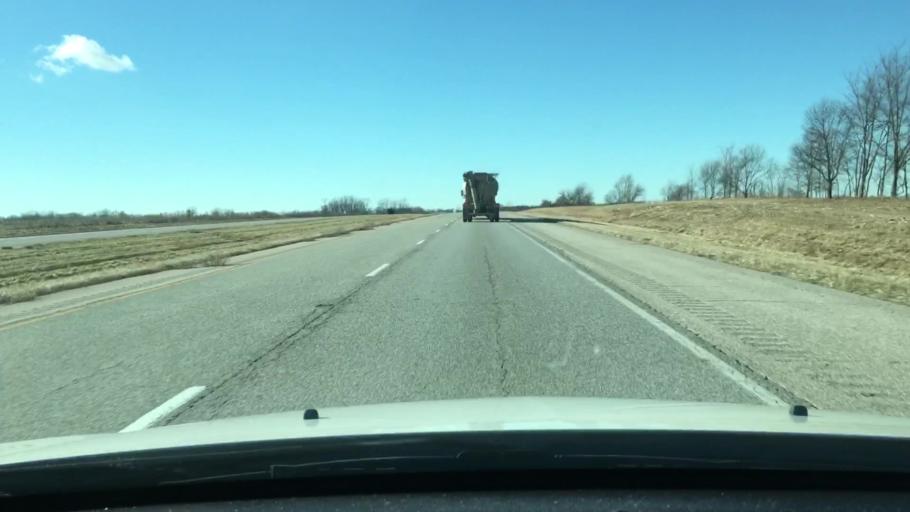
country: US
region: Illinois
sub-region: Pike County
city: Griggsville
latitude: 39.6783
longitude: -90.7055
